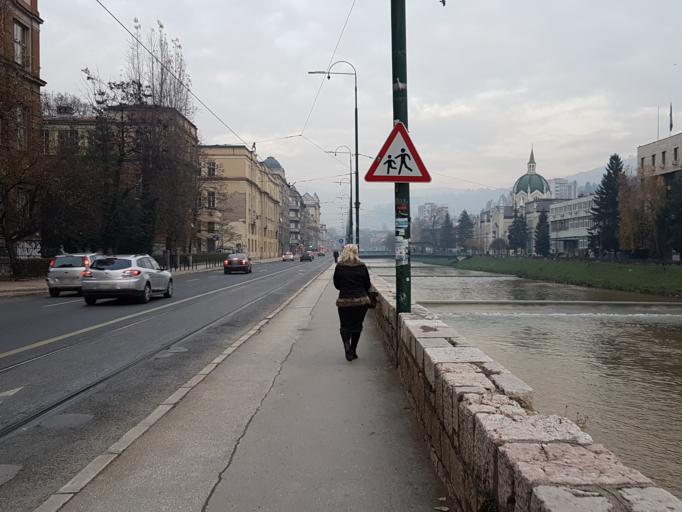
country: BA
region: Federation of Bosnia and Herzegovina
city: Kobilja Glava
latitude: 43.8564
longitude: 18.4151
